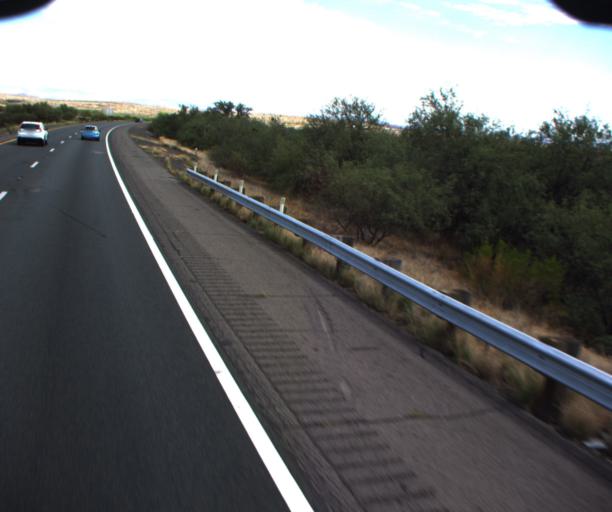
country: US
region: Arizona
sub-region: Yavapai County
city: Spring Valley
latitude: 34.3593
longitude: -112.1170
